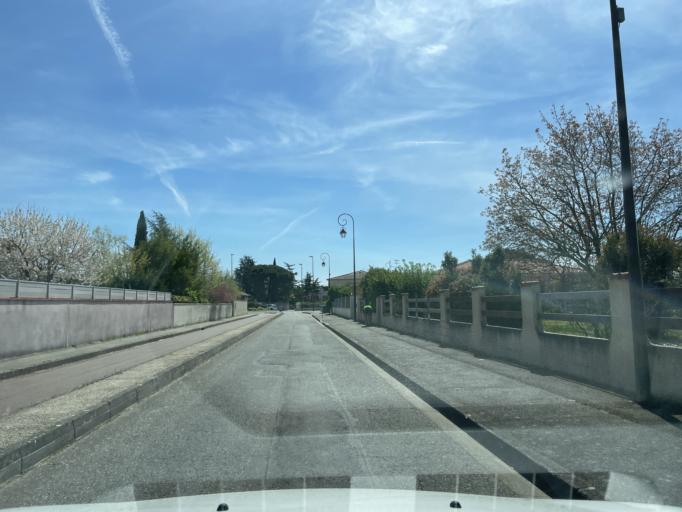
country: FR
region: Midi-Pyrenees
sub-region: Departement de la Haute-Garonne
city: Pibrac
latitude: 43.6159
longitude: 1.2748
